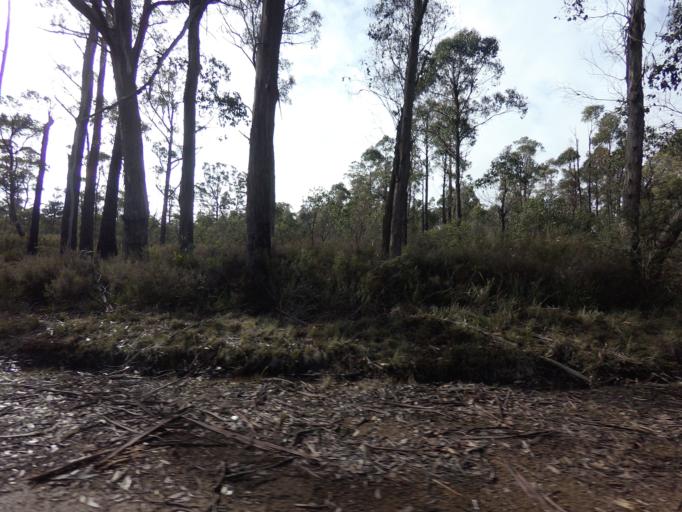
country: AU
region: Tasmania
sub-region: Derwent Valley
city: New Norfolk
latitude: -42.7686
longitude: 146.9002
